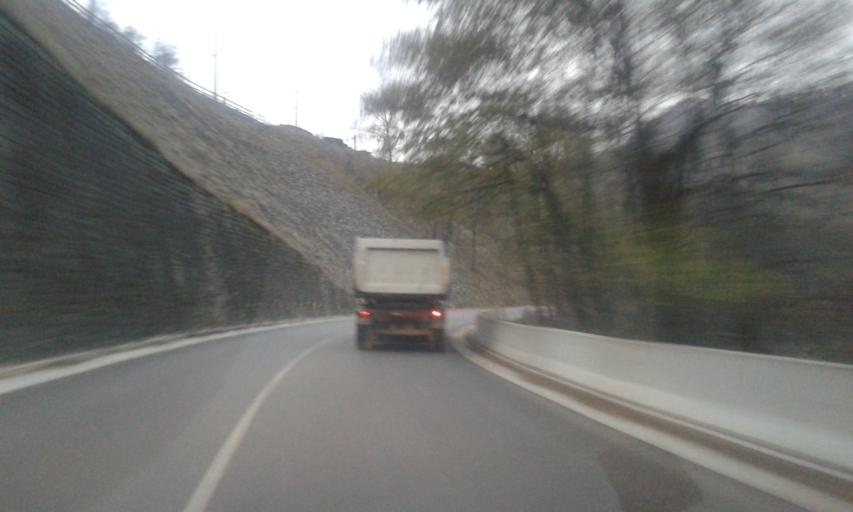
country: RO
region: Gorj
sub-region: Comuna Bumbesti-Jiu
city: Bumbesti-Jiu
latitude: 45.2226
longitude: 23.3831
